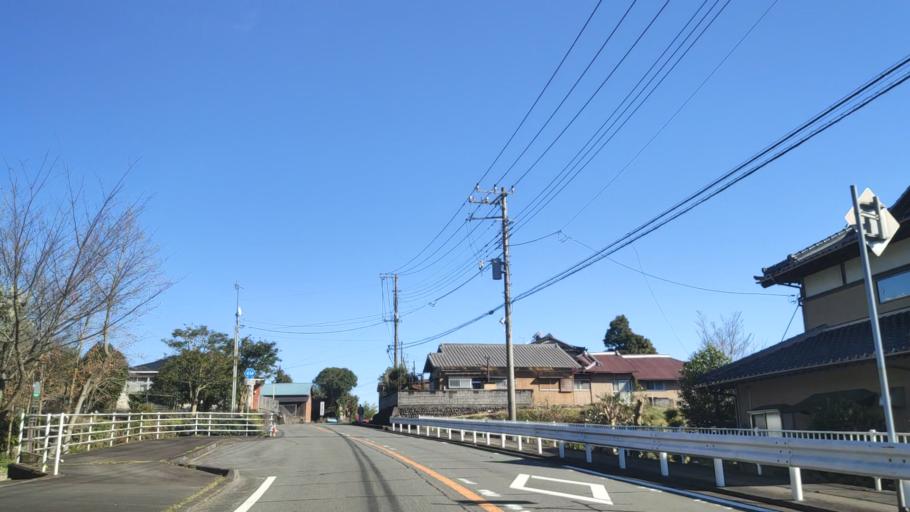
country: JP
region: Shizuoka
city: Fujinomiya
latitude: 35.3110
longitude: 138.5772
